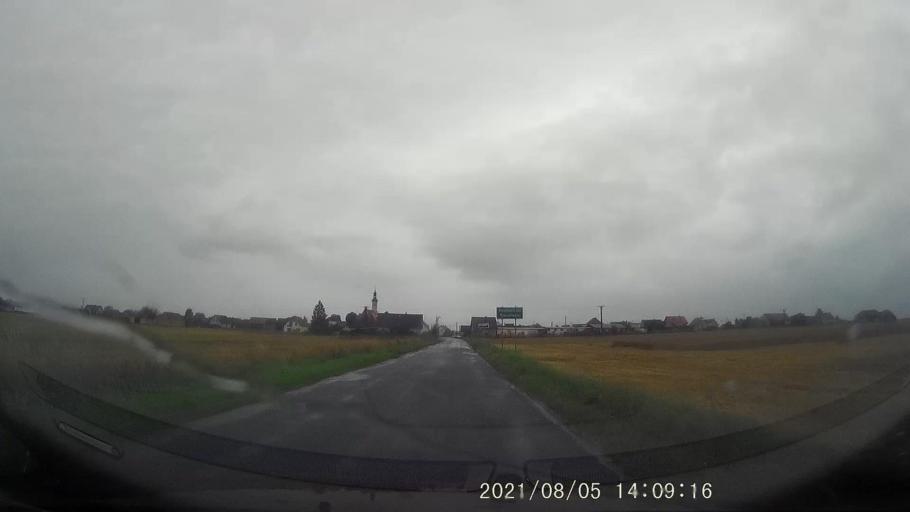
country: PL
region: Opole Voivodeship
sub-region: Powiat krapkowicki
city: Strzeleczki
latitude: 50.4698
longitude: 17.8008
